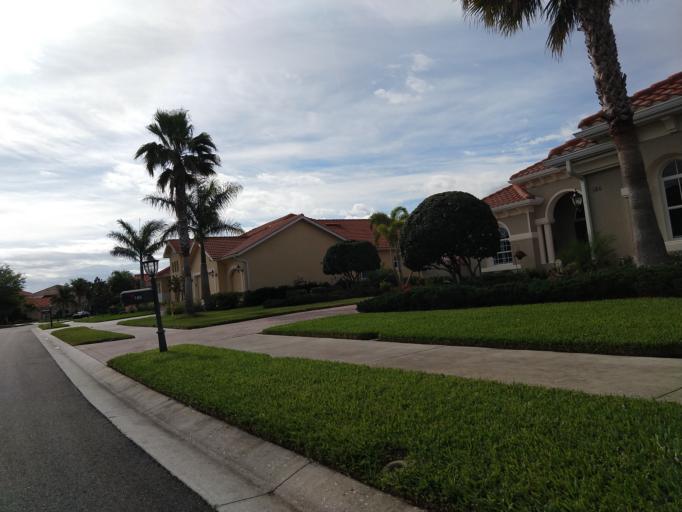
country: US
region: Florida
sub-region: Sarasota County
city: Plantation
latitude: 27.1438
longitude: -82.3664
